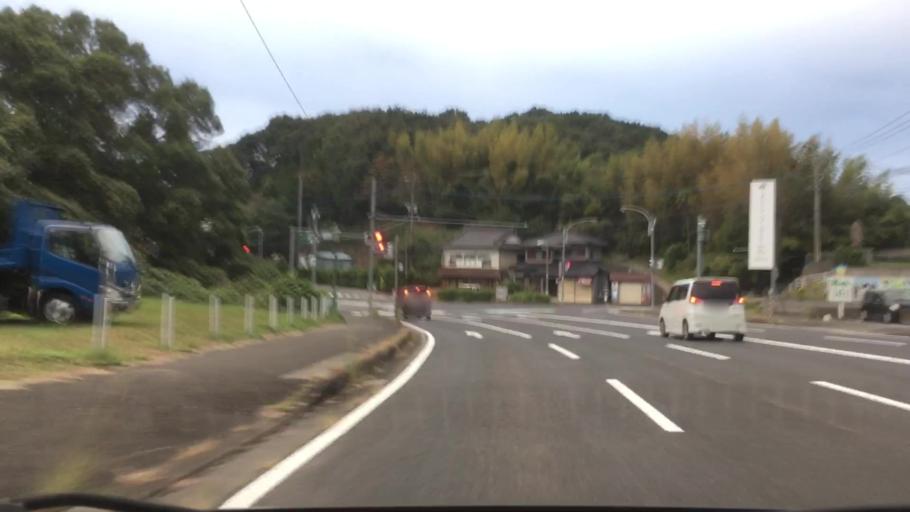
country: JP
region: Nagasaki
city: Sasebo
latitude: 33.0436
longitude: 129.7426
